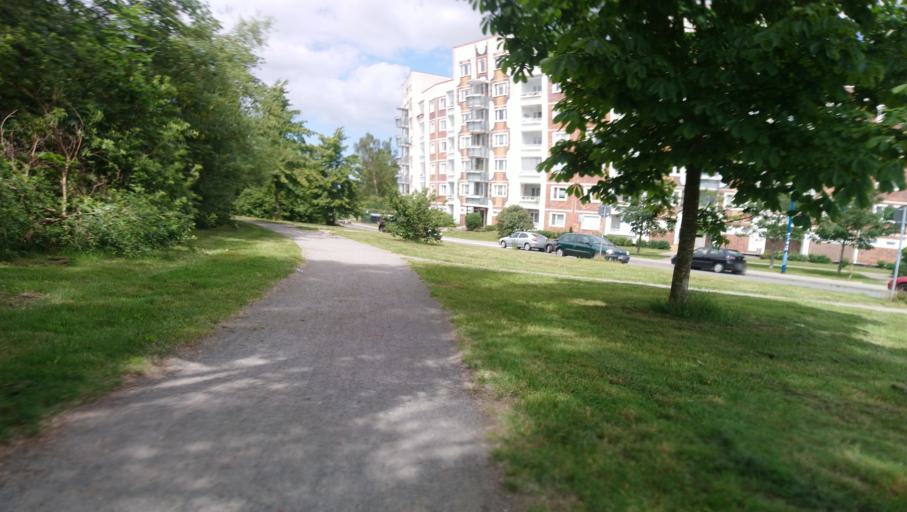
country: DE
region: Mecklenburg-Vorpommern
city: Warnemuende
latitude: 54.1265
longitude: 12.0684
